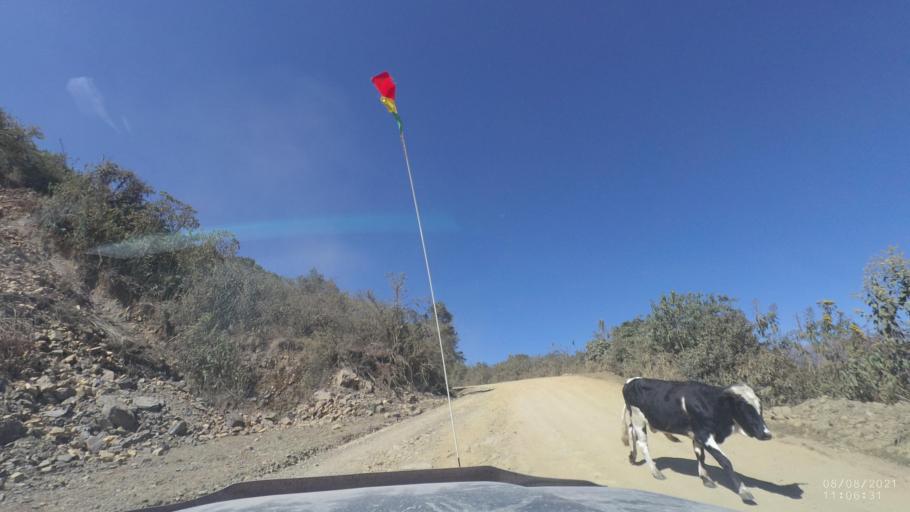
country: BO
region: Cochabamba
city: Colchani
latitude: -16.7634
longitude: -66.6840
